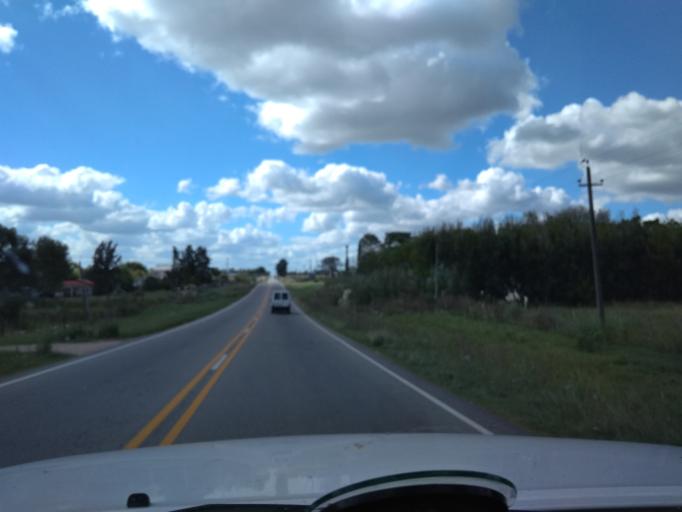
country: UY
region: Canelones
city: Joaquin Suarez
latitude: -34.6940
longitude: -56.0554
